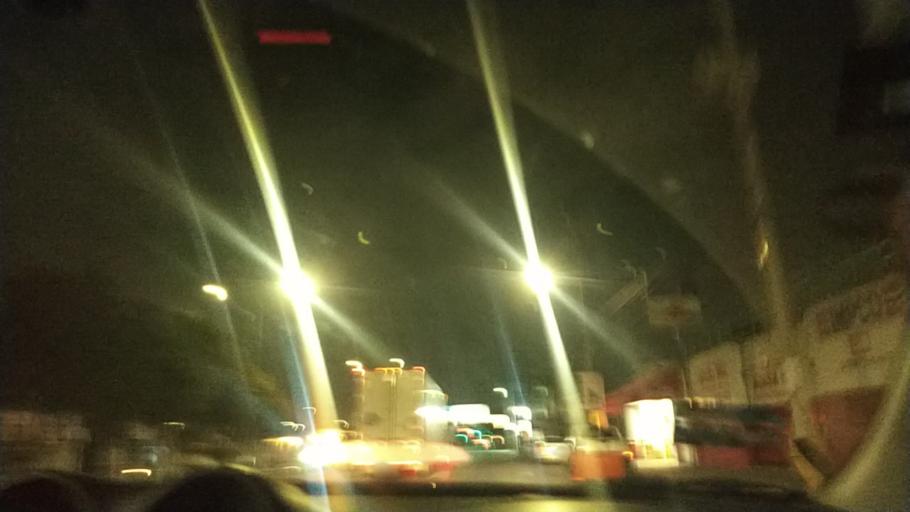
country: MX
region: Mexico
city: Ecatepec
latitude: 19.6209
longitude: -99.0707
